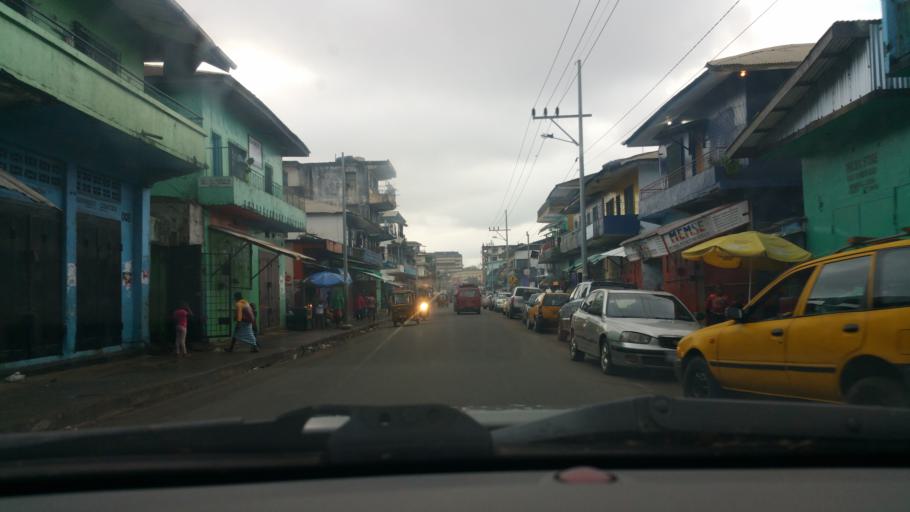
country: LR
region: Montserrado
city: Monrovia
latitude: 6.3091
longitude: -10.8001
